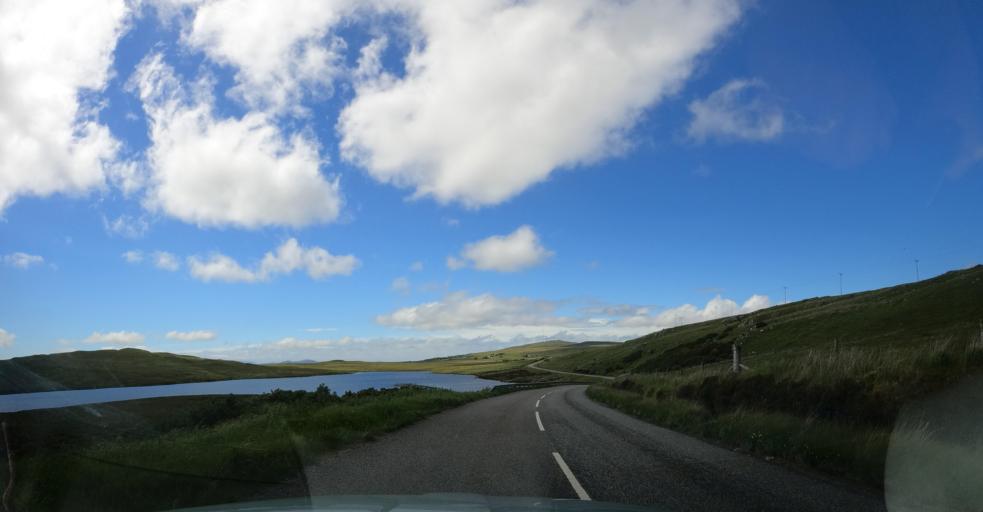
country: GB
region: Scotland
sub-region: Eilean Siar
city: Stornoway
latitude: 58.1586
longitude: -6.5274
